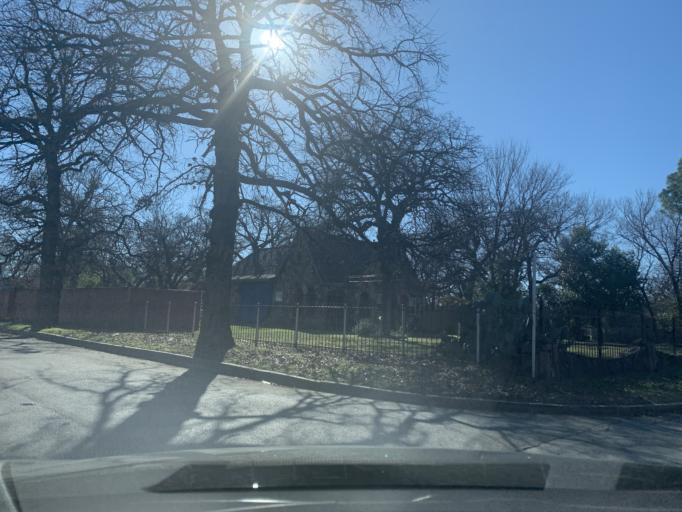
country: US
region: Texas
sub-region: Tarrant County
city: Haltom City
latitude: 32.7818
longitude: -97.2849
